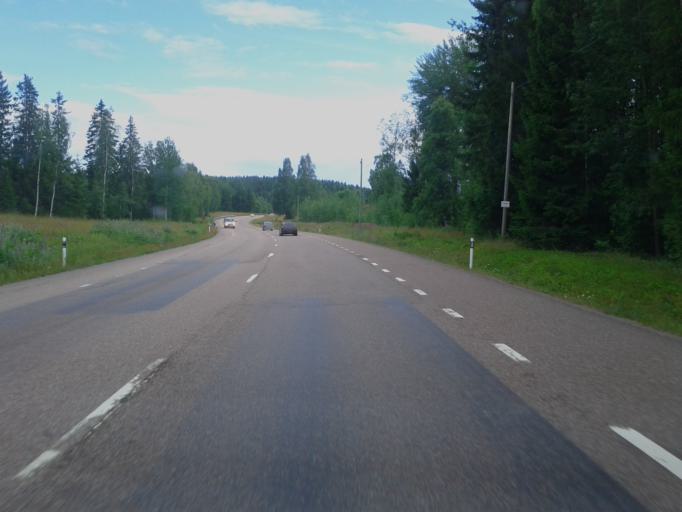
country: SE
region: Dalarna
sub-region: Faluns Kommun
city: Bjursas
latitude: 60.7215
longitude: 15.4514
